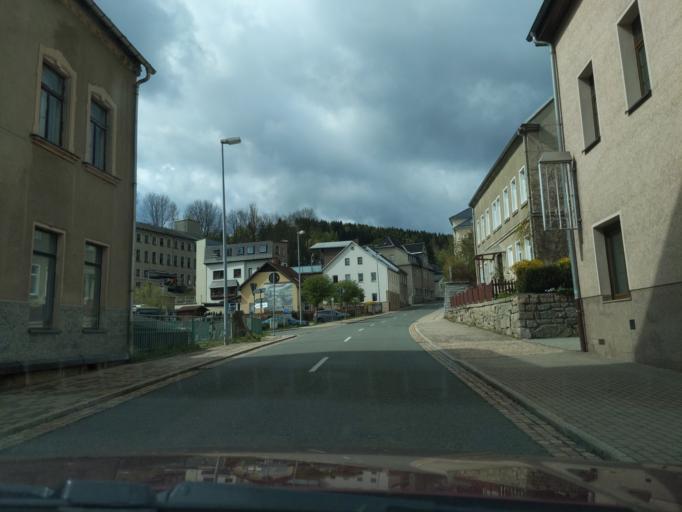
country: DE
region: Saxony
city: Schoenheide
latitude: 50.5049
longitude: 12.5403
